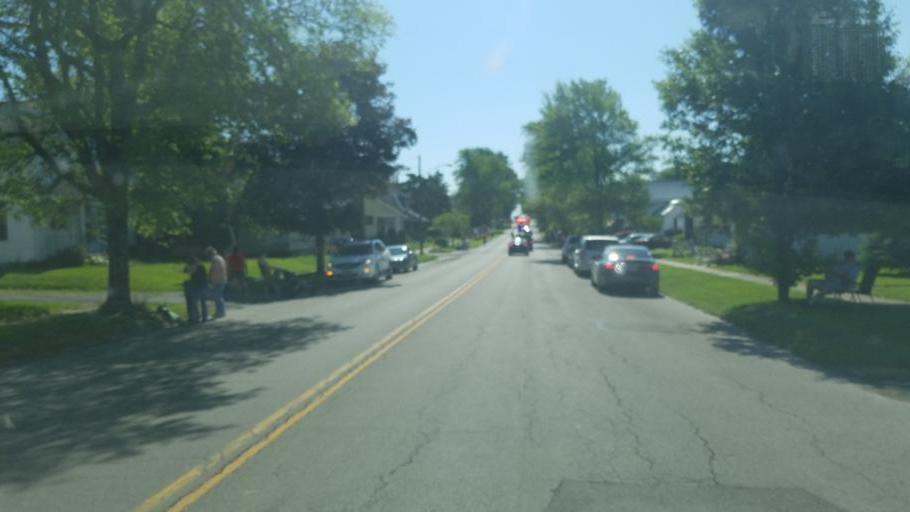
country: US
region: Ohio
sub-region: Hardin County
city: Kenton
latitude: 40.6468
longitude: -83.6031
